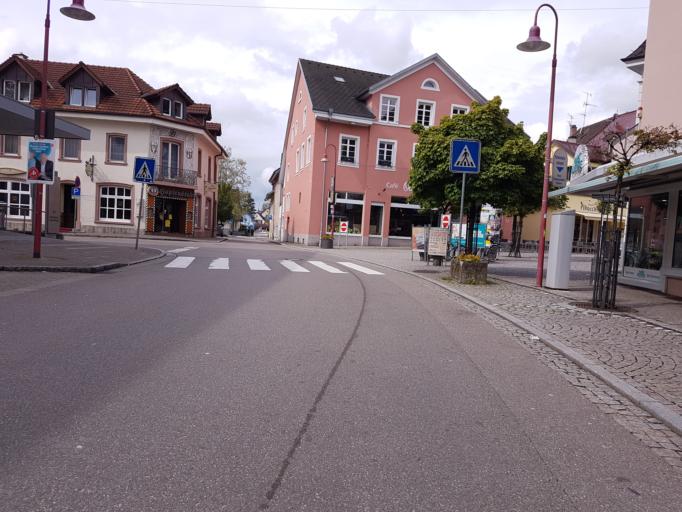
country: DE
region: Baden-Wuerttemberg
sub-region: Freiburg Region
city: Lauchringen
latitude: 47.6351
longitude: 8.2782
